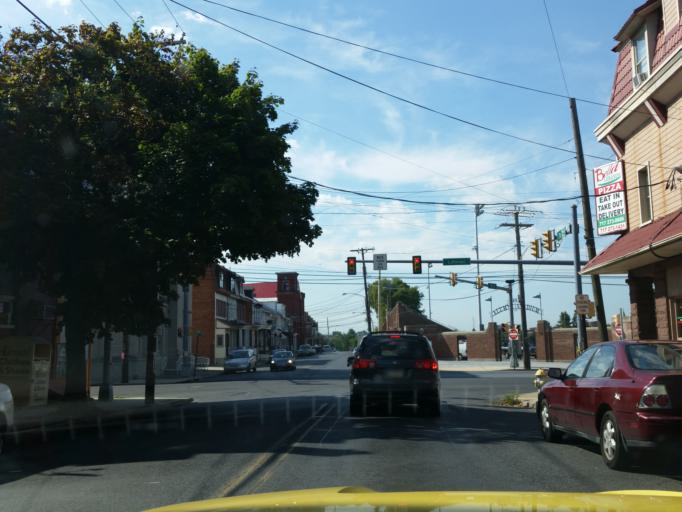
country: US
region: Pennsylvania
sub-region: Lebanon County
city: Lebanon
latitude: 40.3462
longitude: -76.4226
